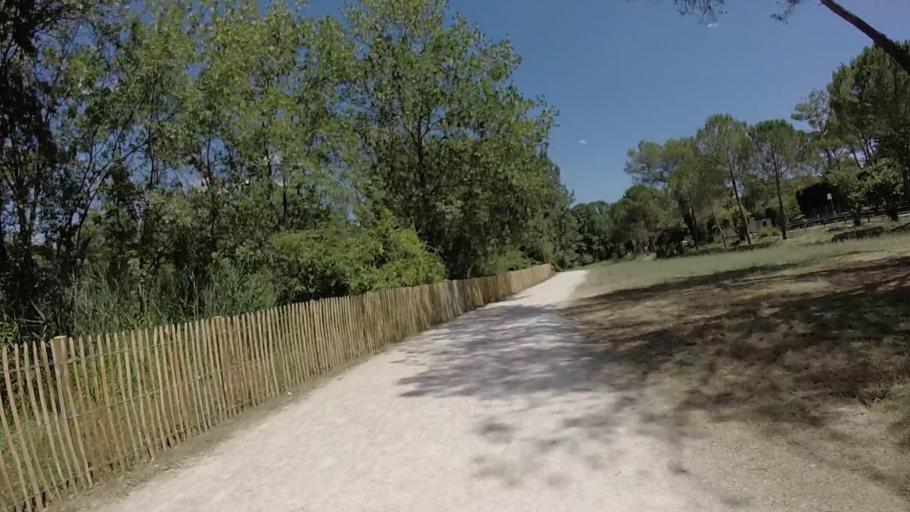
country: FR
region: Provence-Alpes-Cote d'Azur
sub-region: Departement des Alpes-Maritimes
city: Mougins
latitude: 43.5982
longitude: 7.0138
